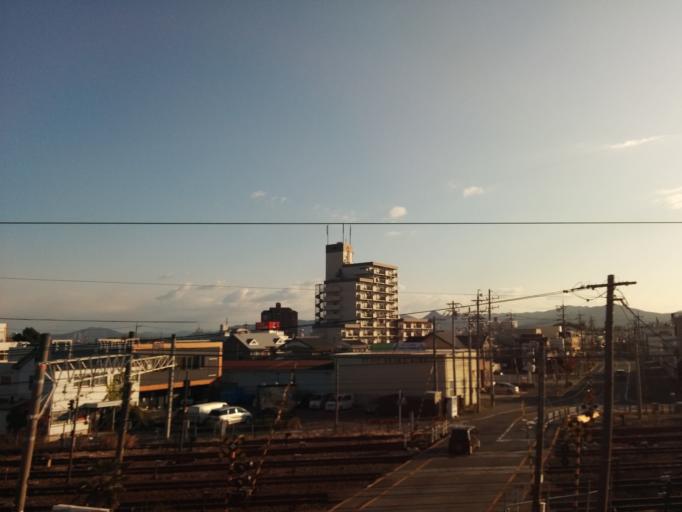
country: JP
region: Aichi
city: Toyohashi
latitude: 34.7724
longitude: 137.3755
